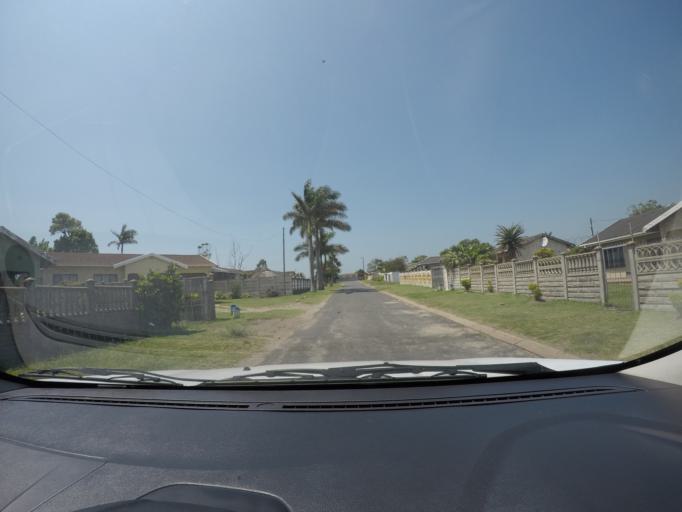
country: ZA
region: KwaZulu-Natal
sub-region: uThungulu District Municipality
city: eSikhawini
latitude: -28.8667
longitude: 31.9177
